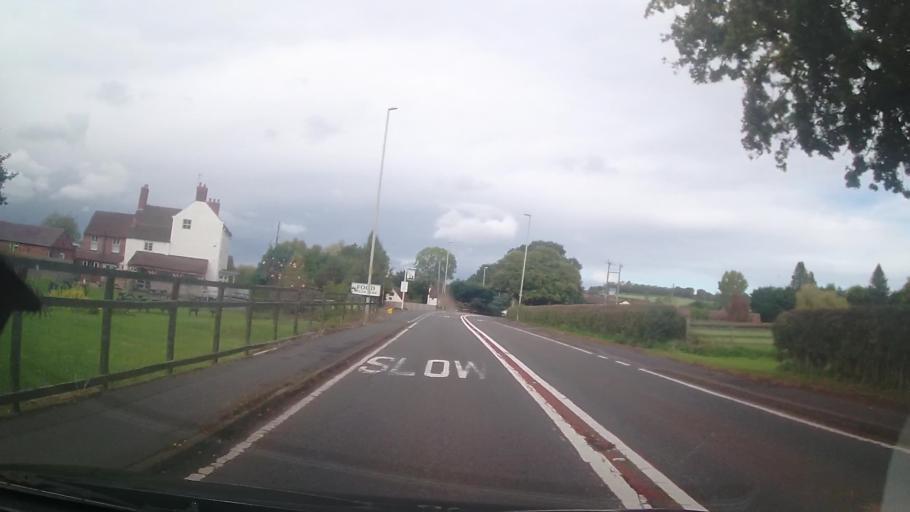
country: GB
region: England
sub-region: Shropshire
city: Alveley
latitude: 52.4623
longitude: -2.3436
